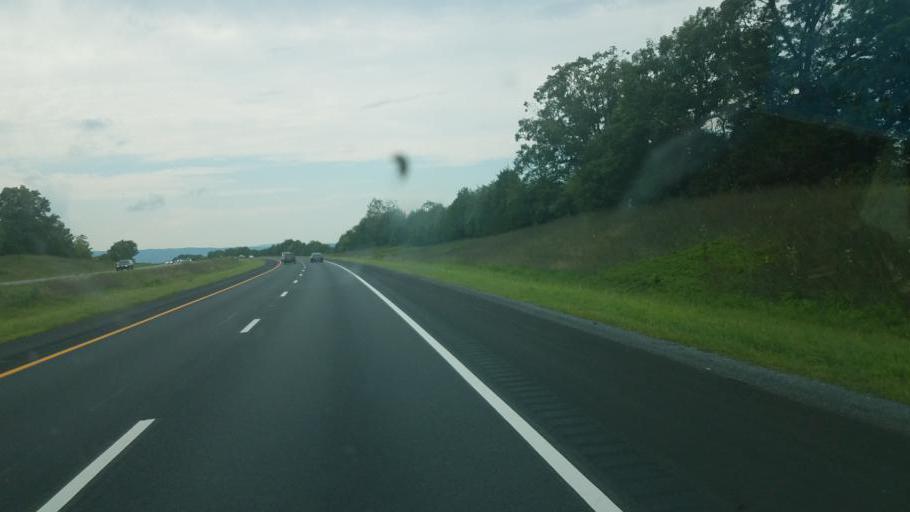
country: US
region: Virginia
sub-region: Frederick County
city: Middletown
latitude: 38.9936
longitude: -78.2508
